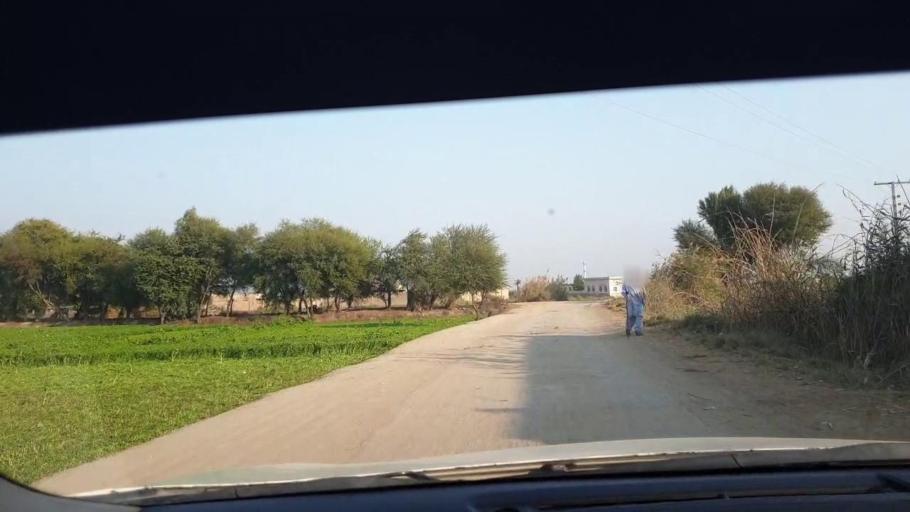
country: PK
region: Sindh
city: Berani
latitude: 25.8414
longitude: 68.7787
